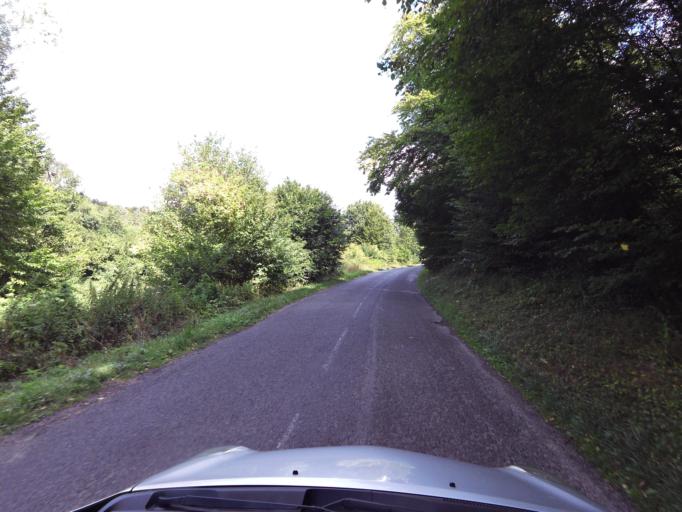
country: FR
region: Picardie
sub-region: Departement de l'Aisne
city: La Ferte-Milon
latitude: 49.2518
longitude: 3.1954
